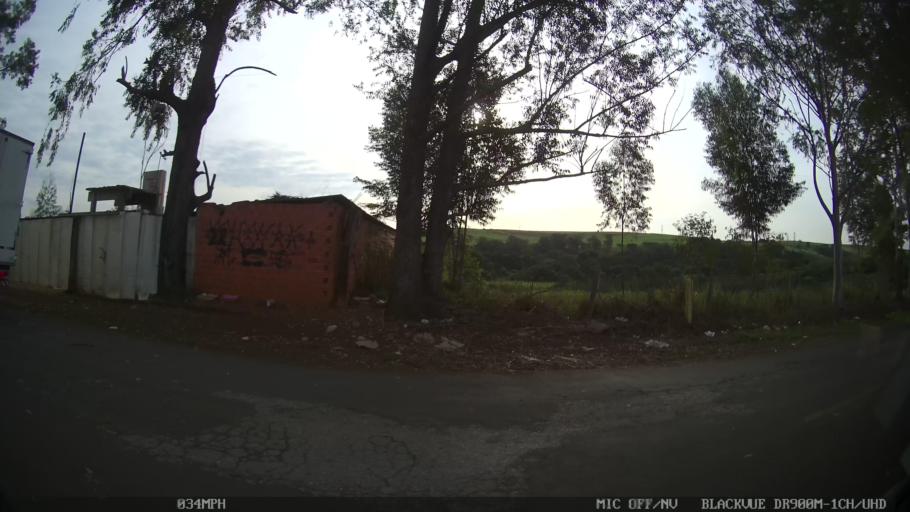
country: BR
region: Sao Paulo
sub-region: Piracicaba
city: Piracicaba
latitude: -22.6931
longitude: -47.5831
